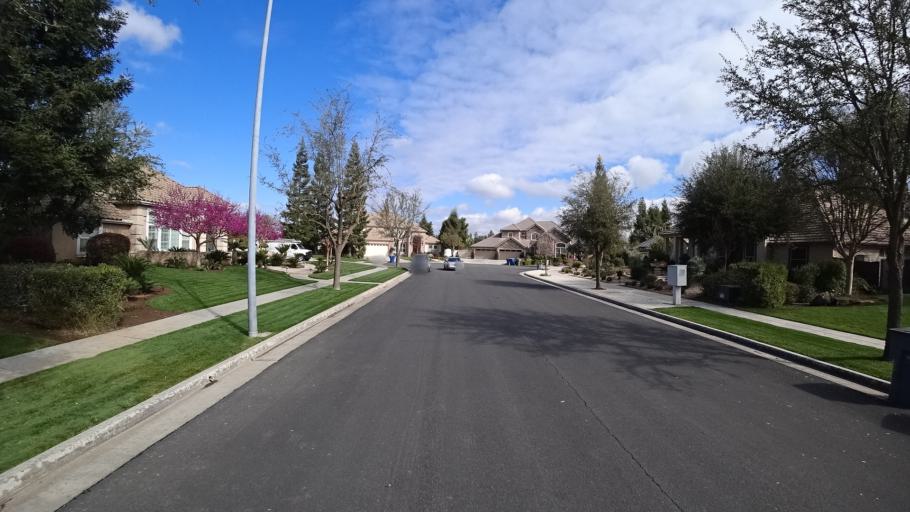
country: US
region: California
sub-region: Fresno County
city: Fresno
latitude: 36.8344
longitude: -119.8618
